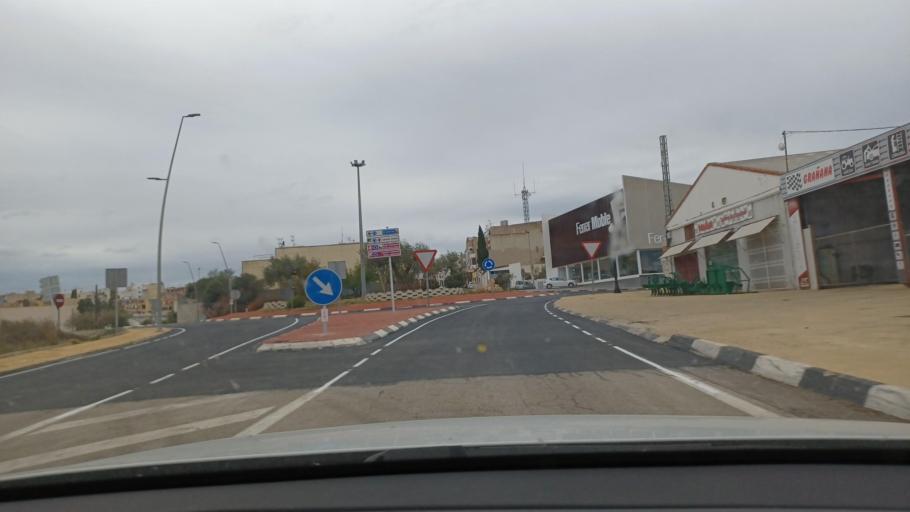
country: ES
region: Valencia
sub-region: Provincia de Castello
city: Traiguera
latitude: 40.5252
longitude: 0.2953
